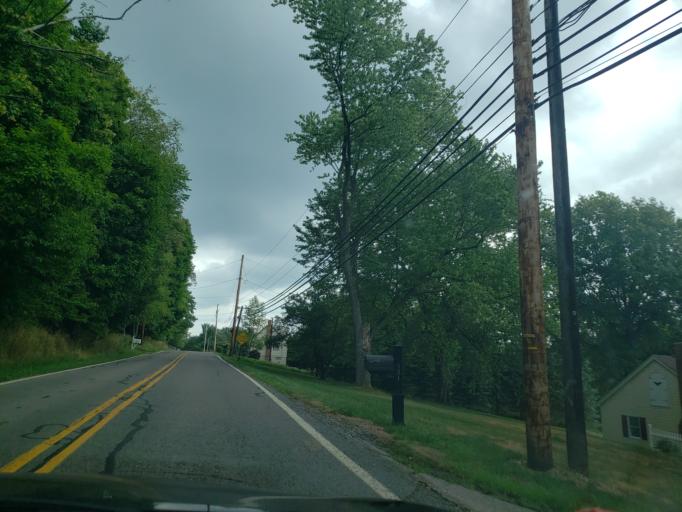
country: US
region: Pennsylvania
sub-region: Allegheny County
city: Coraopolis
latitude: 40.5313
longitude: -80.1474
